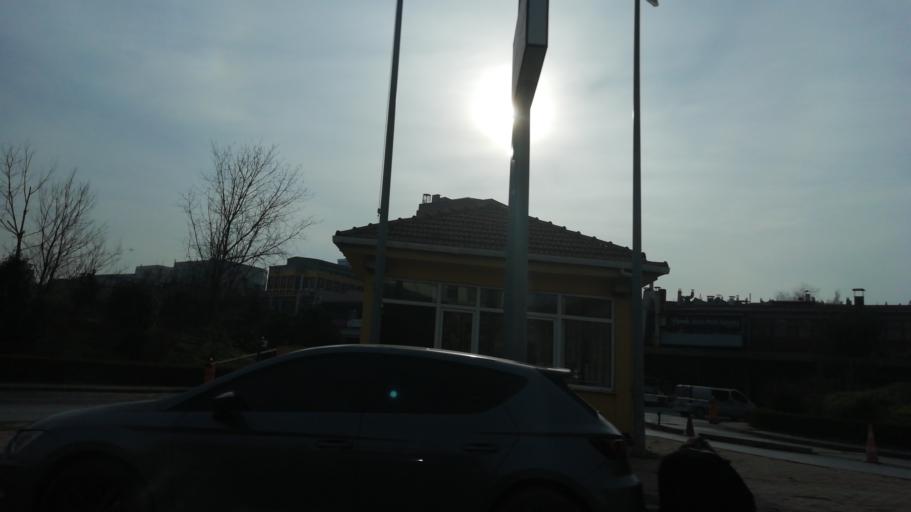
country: TR
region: Istanbul
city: Basaksehir
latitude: 41.0847
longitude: 28.8084
